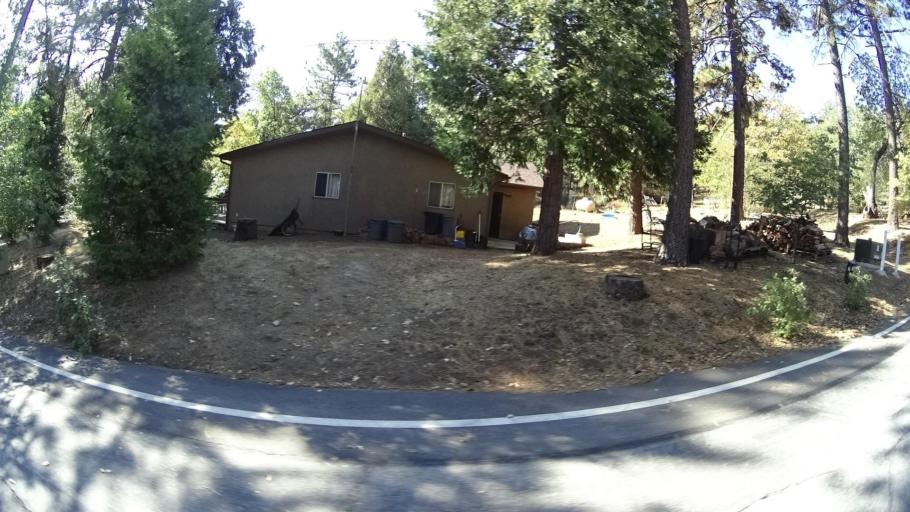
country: US
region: California
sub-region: San Diego County
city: Pine Valley
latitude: 32.8631
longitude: -116.4216
